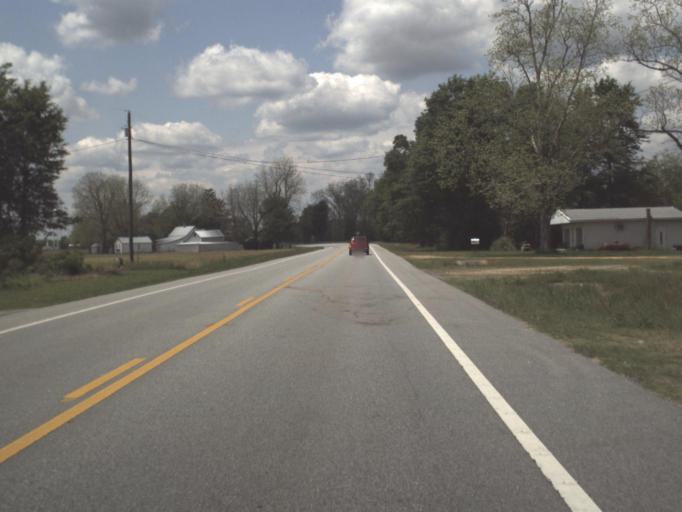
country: US
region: Alabama
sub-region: Escambia County
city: Atmore
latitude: 30.8921
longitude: -87.4674
